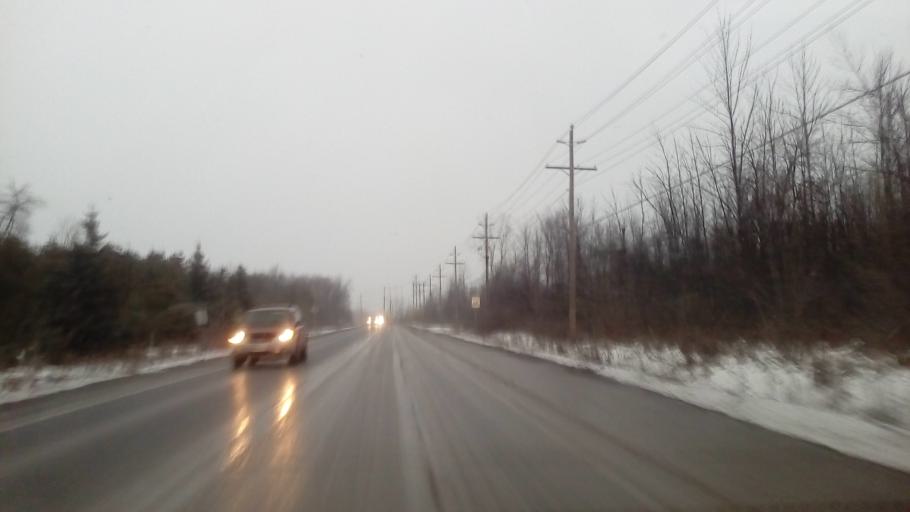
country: CA
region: Ontario
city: Ottawa
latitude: 45.4494
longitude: -75.5771
